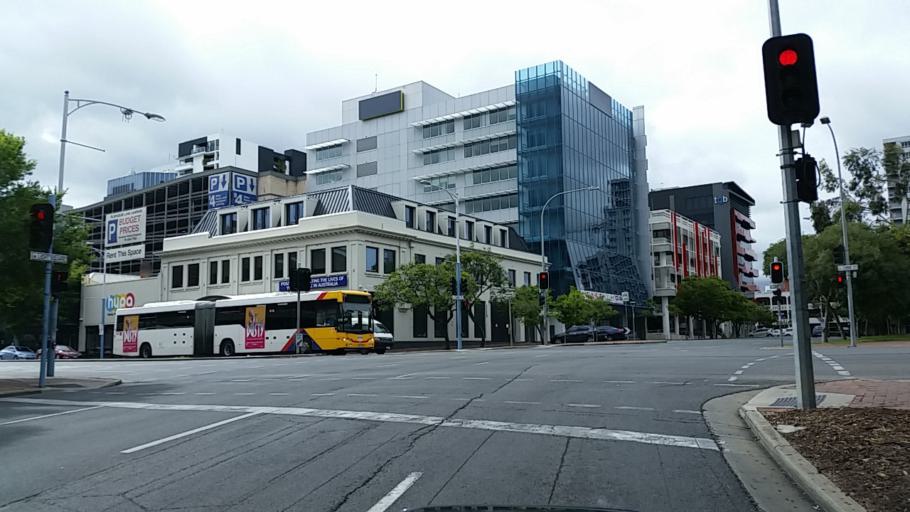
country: AU
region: South Australia
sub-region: Adelaide
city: Adelaide
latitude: -34.9244
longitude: 138.5941
